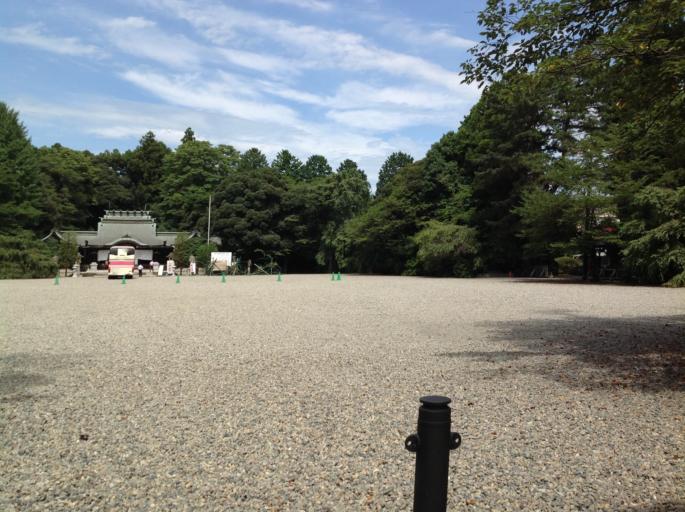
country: JP
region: Tochigi
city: Utsunomiya-shi
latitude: 36.5711
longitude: 139.8599
